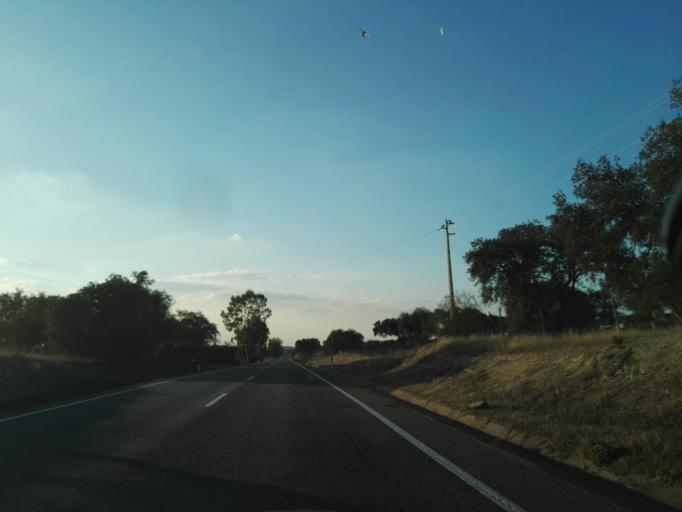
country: PT
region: Evora
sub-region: Arraiolos
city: Arraiolos
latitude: 38.8715
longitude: -7.9602
